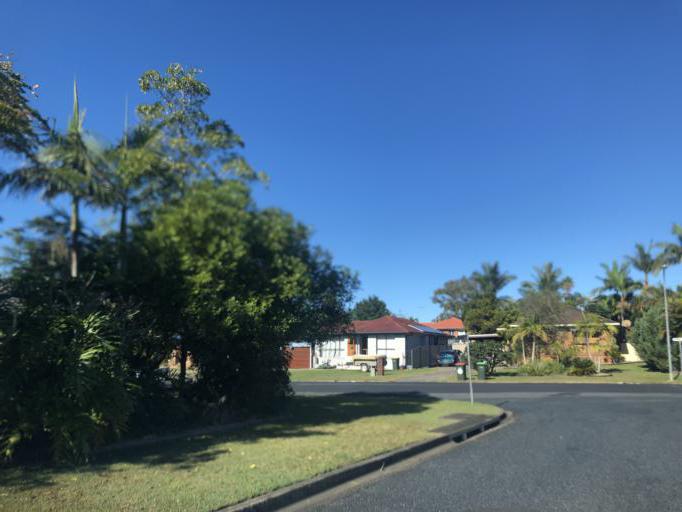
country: AU
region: New South Wales
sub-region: Coffs Harbour
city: Toormina
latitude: -30.3677
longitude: 153.0848
